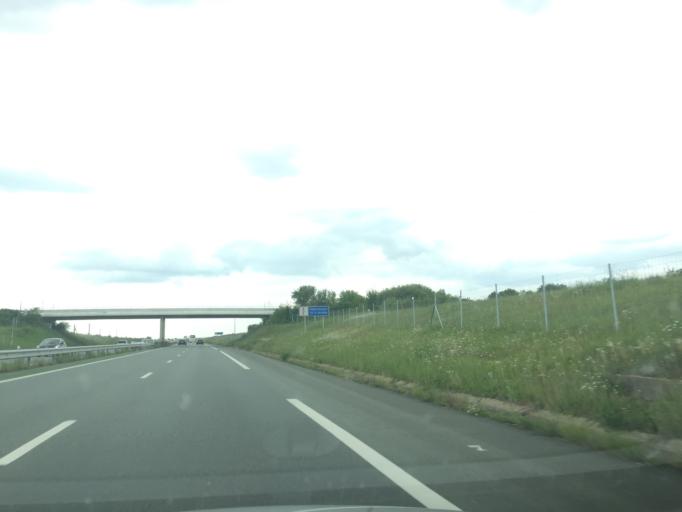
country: FR
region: Pays de la Loire
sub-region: Departement de la Vendee
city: Benet
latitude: 46.4006
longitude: -0.6193
